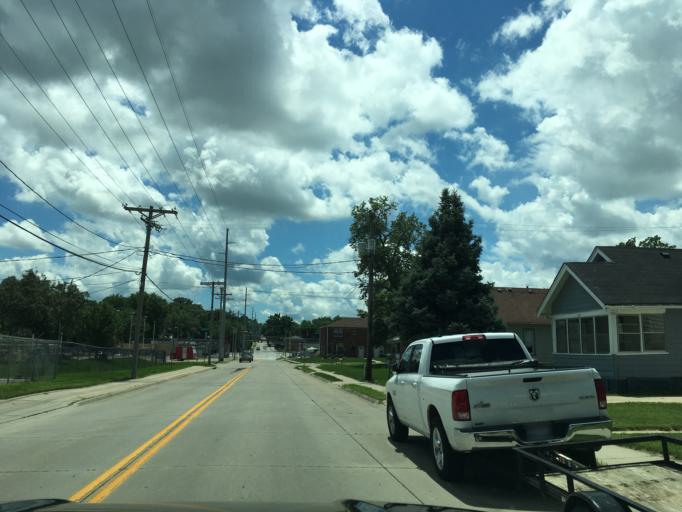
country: US
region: Nebraska
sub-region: Douglas County
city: Omaha
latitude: 41.2479
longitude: -95.9903
